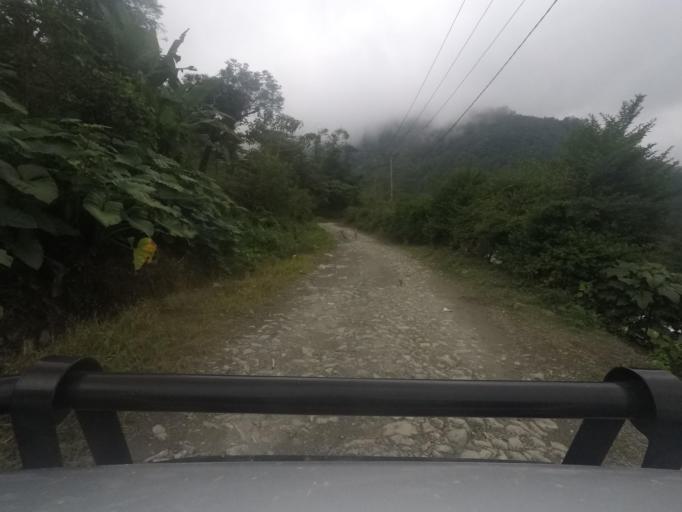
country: TL
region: Bobonaro
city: Maliana
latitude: -9.1417
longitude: 125.2627
